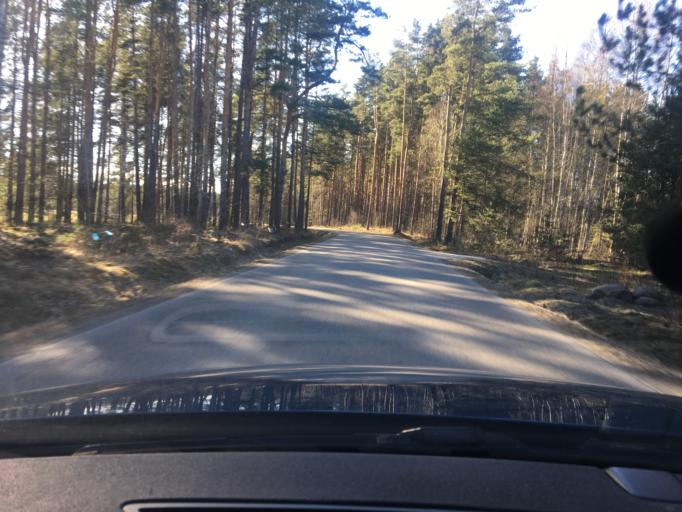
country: LV
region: Salaspils
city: Salaspils
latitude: 56.8669
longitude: 24.3090
